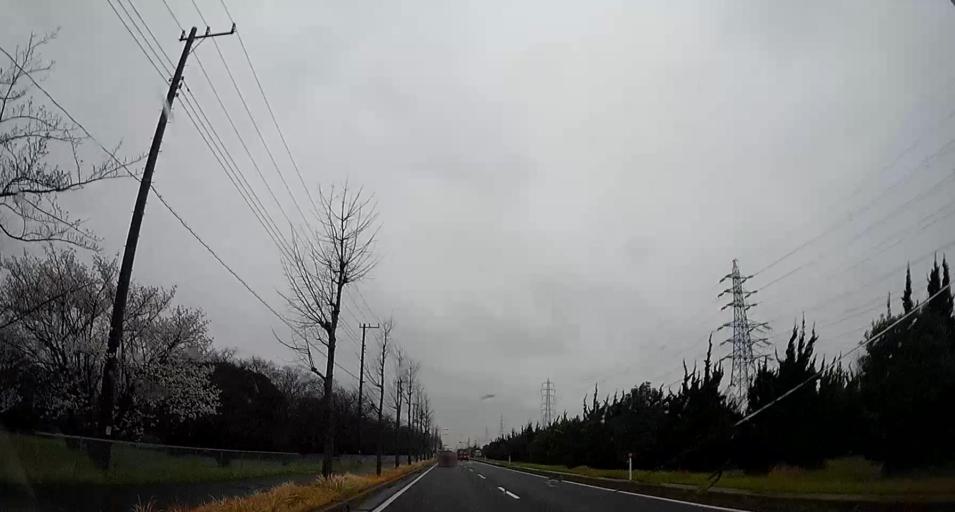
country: JP
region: Chiba
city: Ichihara
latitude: 35.5038
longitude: 140.0514
